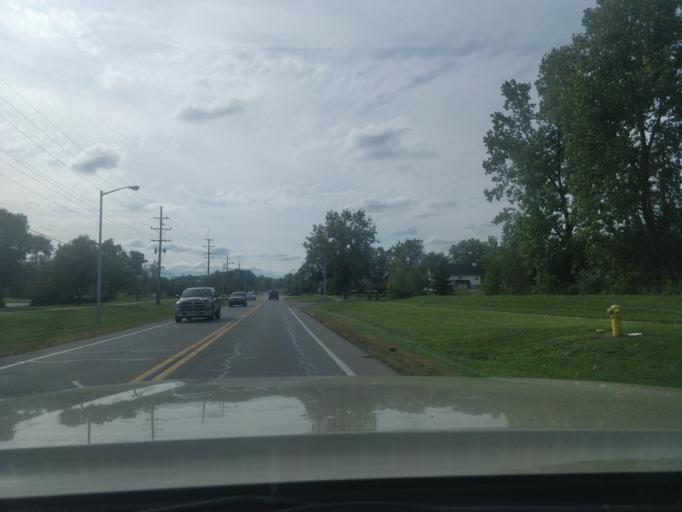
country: US
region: Michigan
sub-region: Wayne County
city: Woodhaven
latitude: 42.1535
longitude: -83.2572
